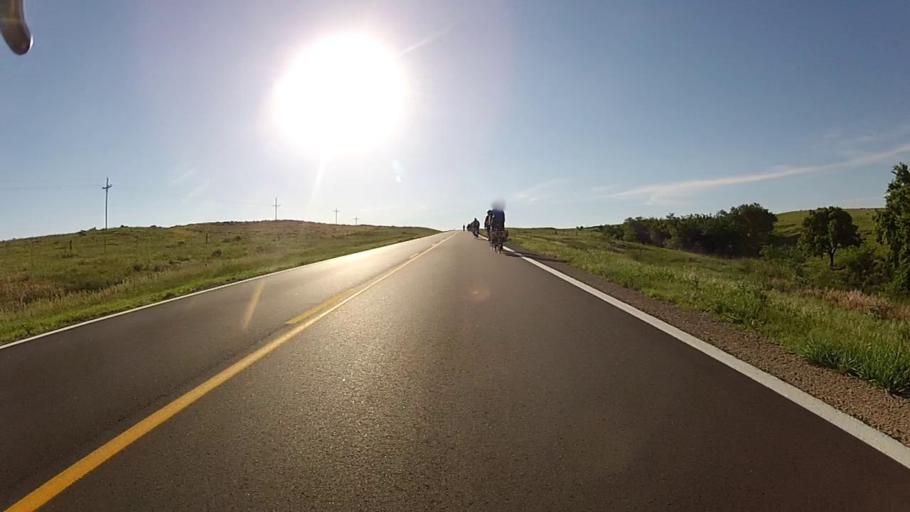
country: US
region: Kansas
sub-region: Comanche County
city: Coldwater
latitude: 37.2806
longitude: -99.0248
